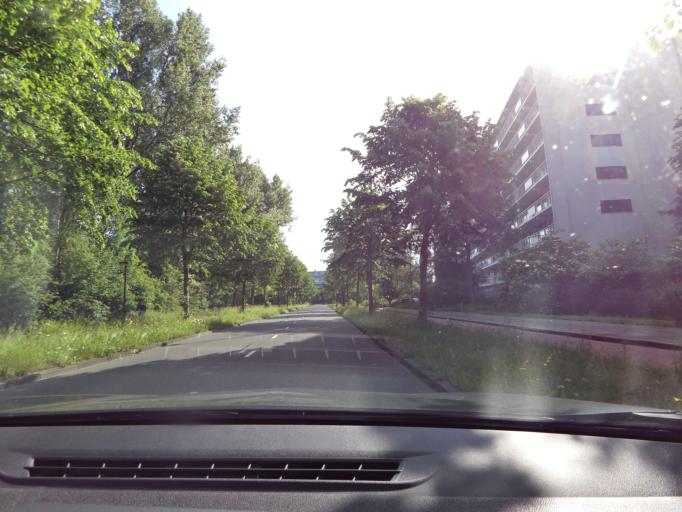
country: NL
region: South Holland
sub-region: Gemeente Vlaardingen
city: Vlaardingen
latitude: 51.9357
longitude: 4.3501
